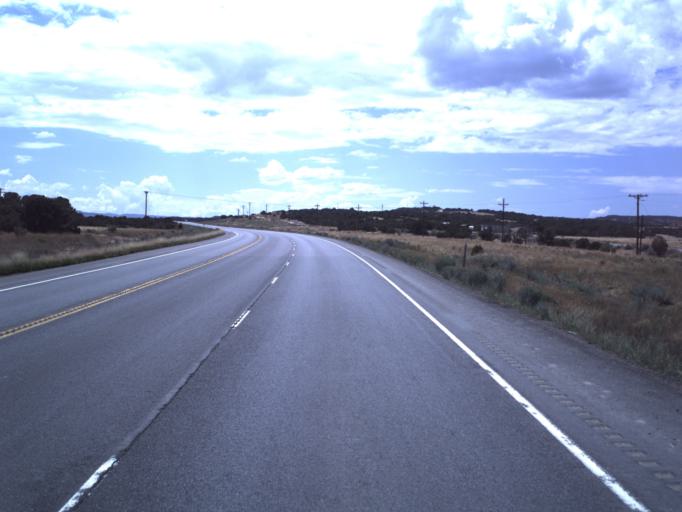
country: US
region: Utah
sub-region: Duchesne County
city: Duchesne
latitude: 40.1778
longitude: -110.5352
